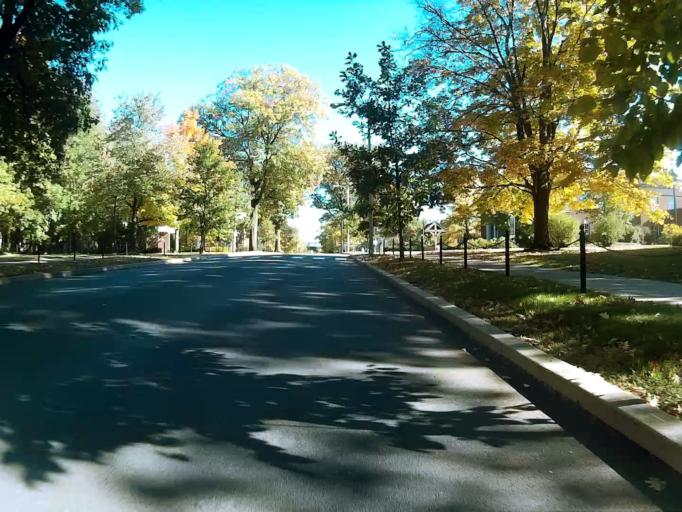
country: US
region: Pennsylvania
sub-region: Centre County
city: State College
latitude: 40.8025
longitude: -77.8648
